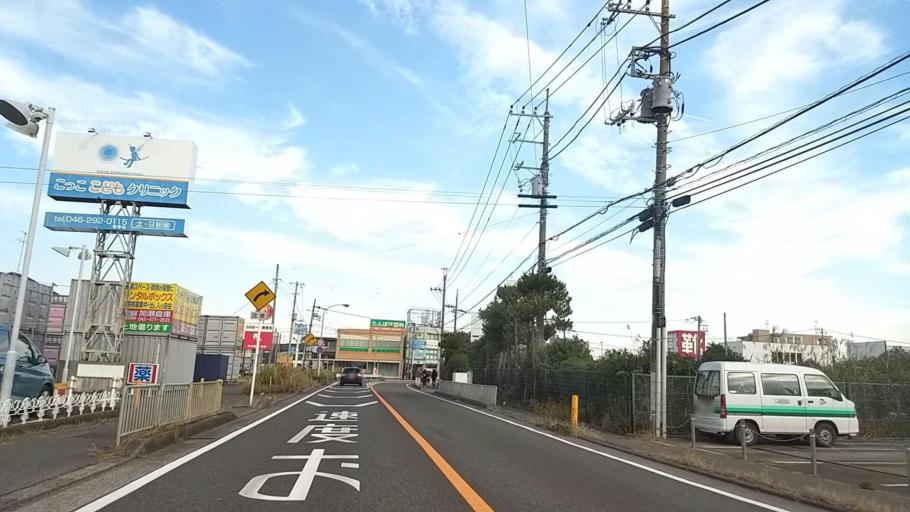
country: JP
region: Kanagawa
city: Atsugi
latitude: 35.4496
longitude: 139.3777
